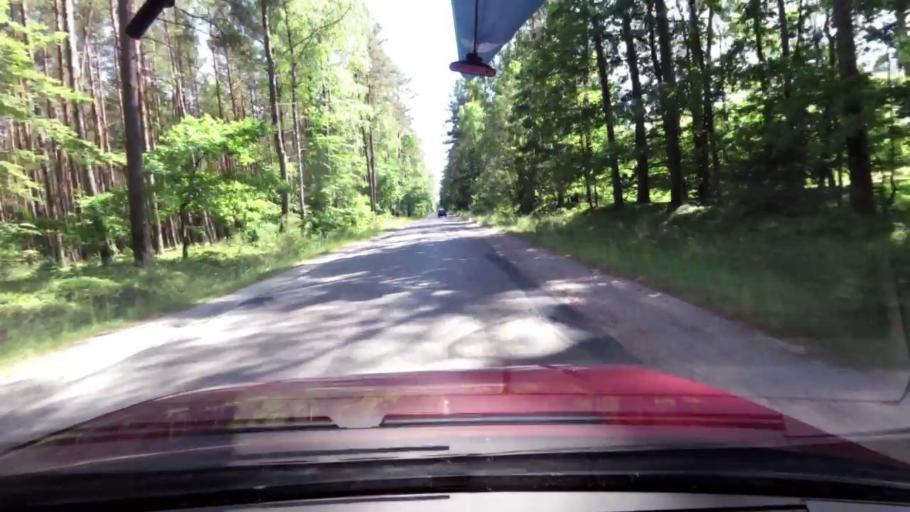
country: PL
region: Pomeranian Voivodeship
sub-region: Powiat slupski
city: Kepice
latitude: 54.3202
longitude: 16.9620
